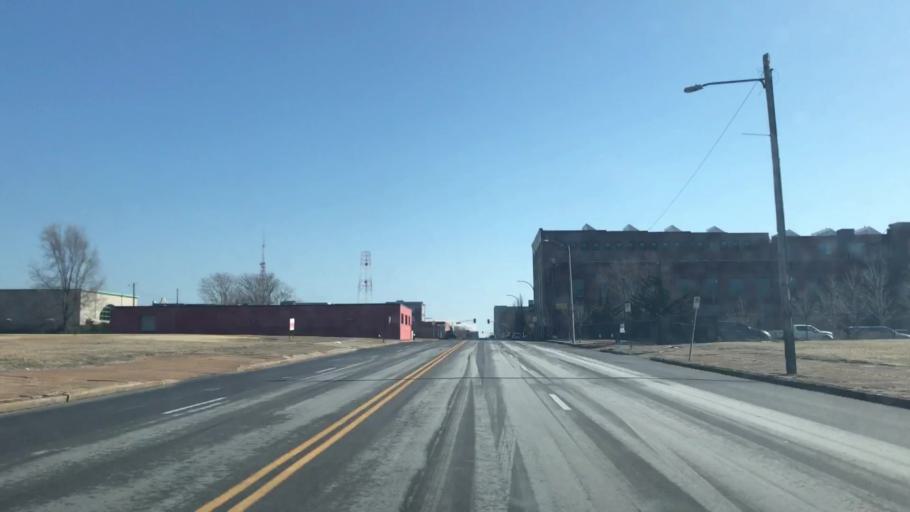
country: US
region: Missouri
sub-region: City of Saint Louis
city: St. Louis
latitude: 38.6362
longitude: -90.2100
